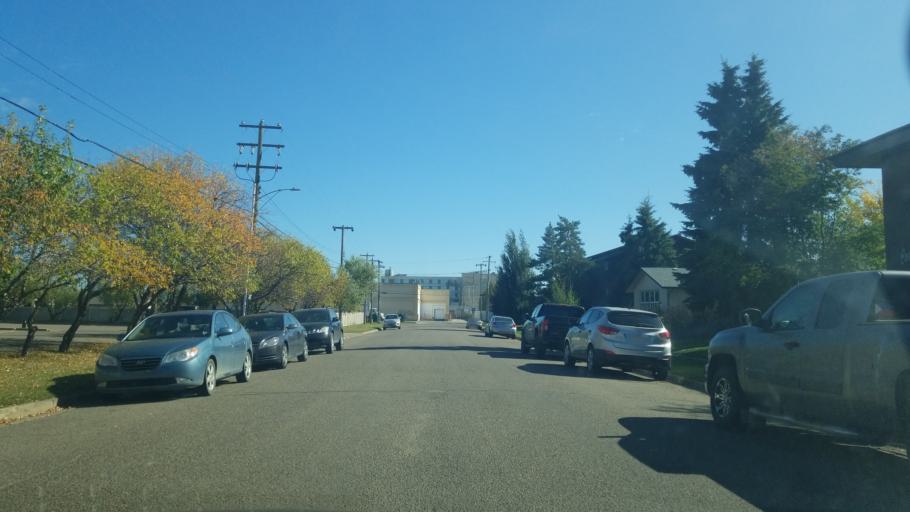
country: CA
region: Saskatchewan
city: Lloydminster
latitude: 53.2770
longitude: -110.0216
